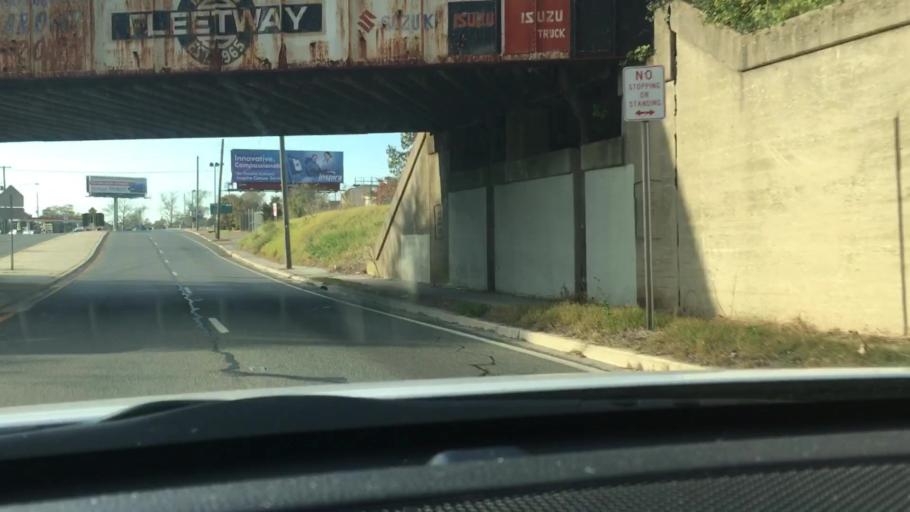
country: US
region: New Jersey
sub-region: Atlantic County
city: Pleasantville
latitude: 39.3912
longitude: -74.5269
